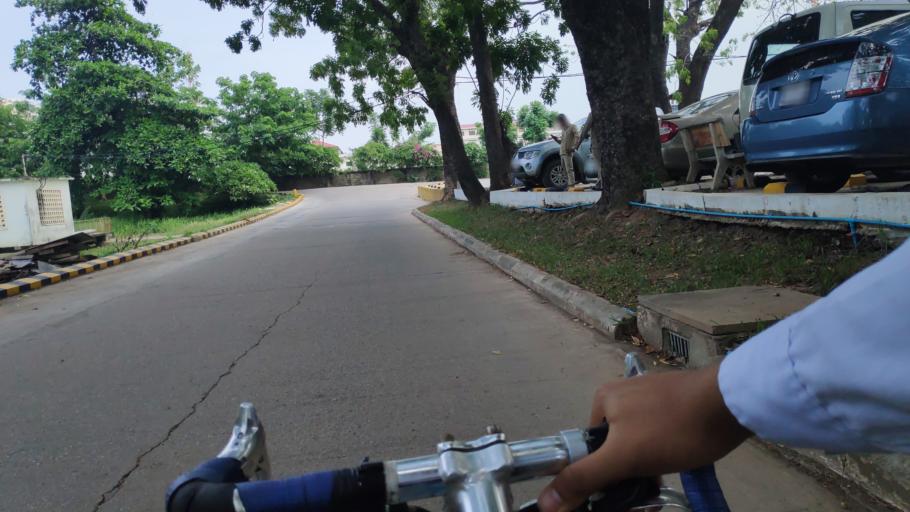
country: KH
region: Phnom Penh
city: Phnom Penh
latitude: 11.5699
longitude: 104.8969
